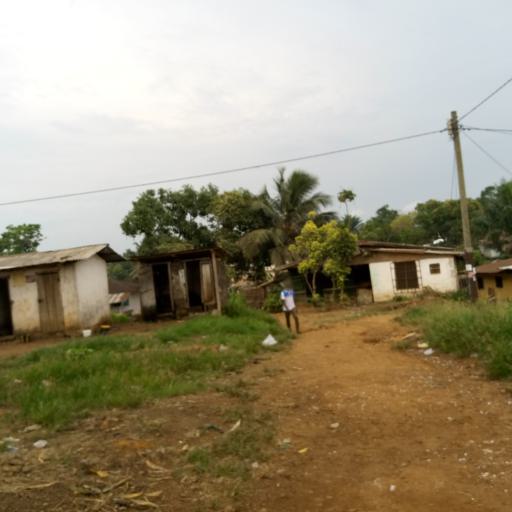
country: LR
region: Montserrado
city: Monrovia
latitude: 6.3004
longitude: -10.6884
